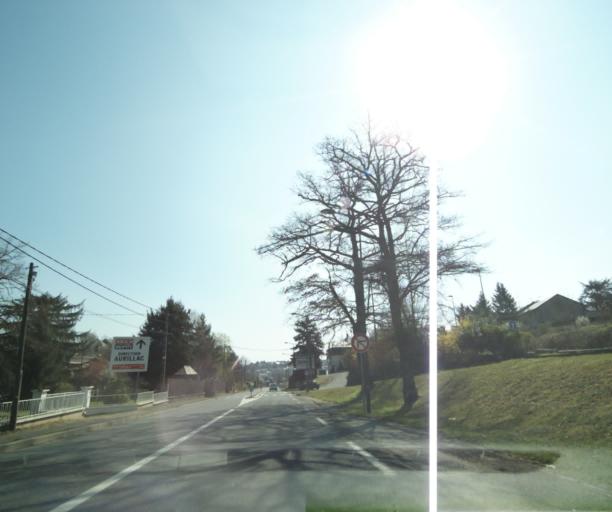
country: FR
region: Midi-Pyrenees
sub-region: Departement de l'Aveyron
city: Olemps
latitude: 44.3632
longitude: 2.5578
